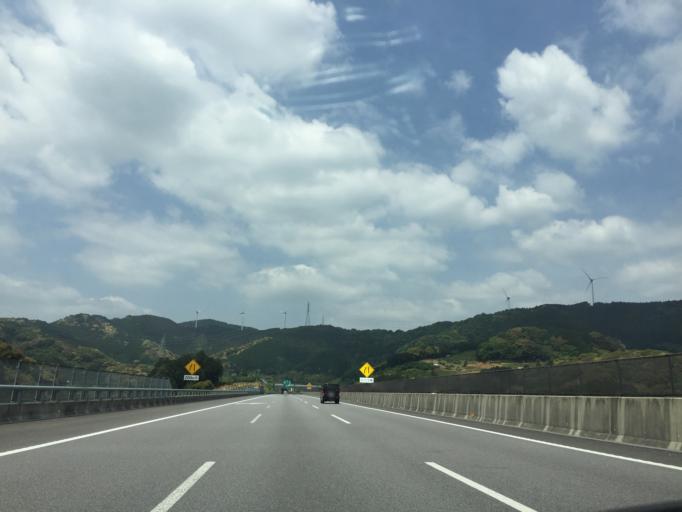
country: JP
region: Shizuoka
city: Hamakita
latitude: 34.8489
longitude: 137.7243
